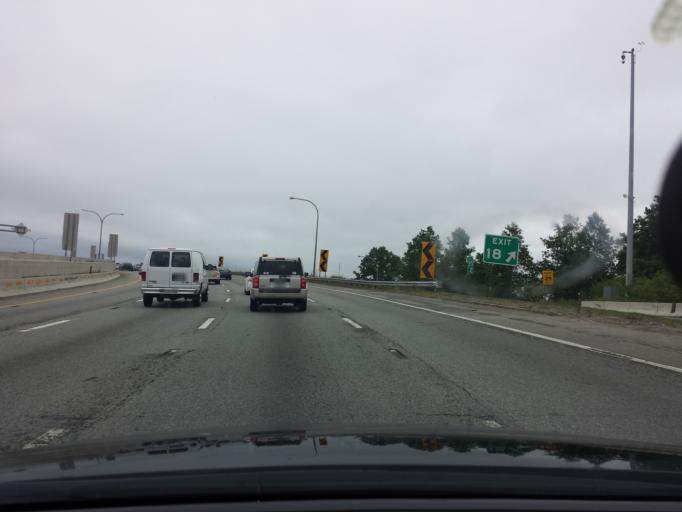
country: US
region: Rhode Island
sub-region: Providence County
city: Providence
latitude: 41.7986
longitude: -71.4026
